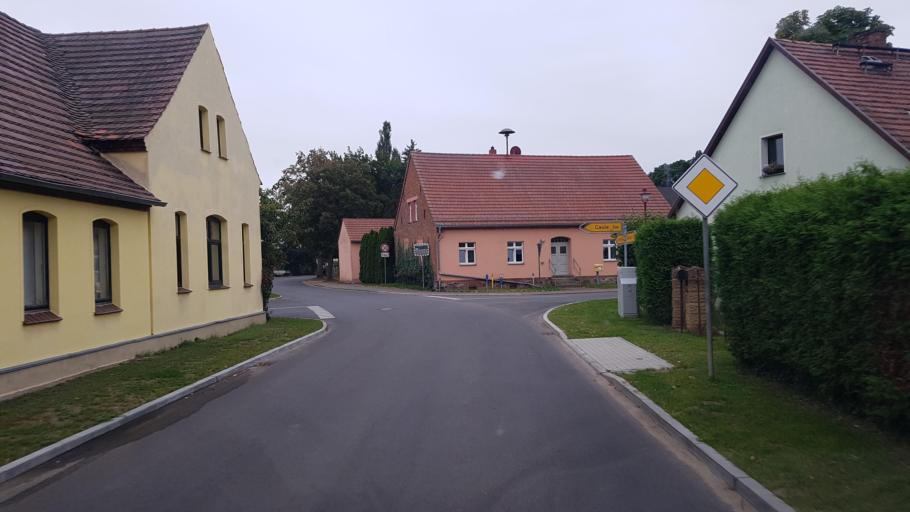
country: DE
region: Brandenburg
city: Drahnsdorf
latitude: 51.8940
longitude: 13.6446
